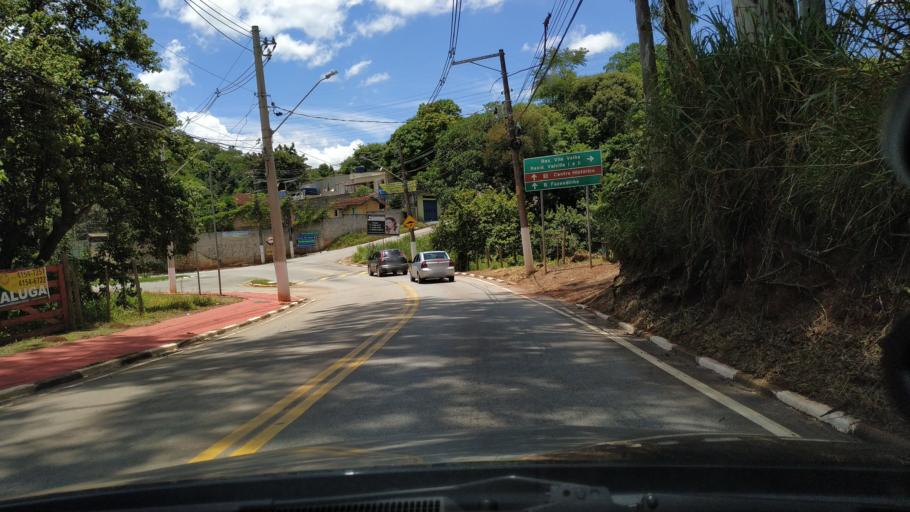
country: BR
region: Sao Paulo
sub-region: Santana De Parnaiba
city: Santana de Parnaiba
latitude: -23.4420
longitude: -46.9072
